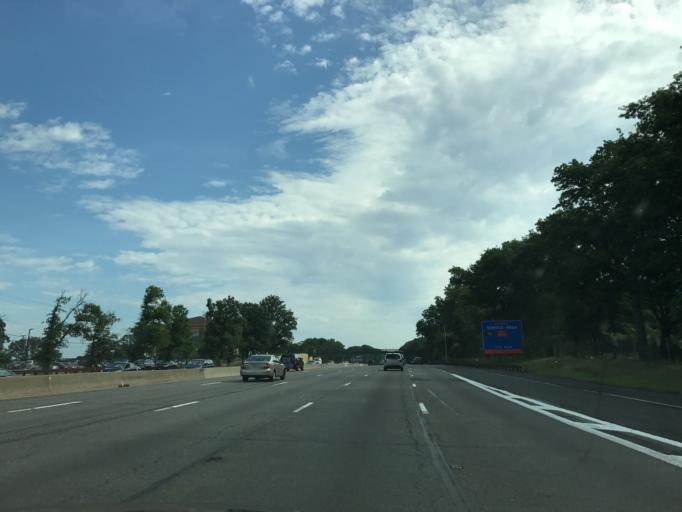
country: US
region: New Jersey
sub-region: Union County
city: Kenilworth
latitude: 40.6819
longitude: -74.2771
